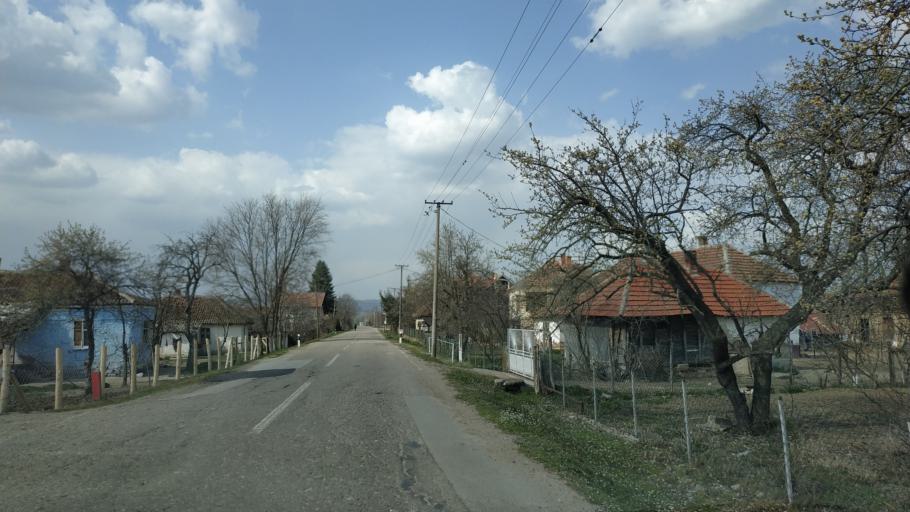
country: RS
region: Central Serbia
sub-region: Nisavski Okrug
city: Razanj
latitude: 43.5855
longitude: 21.5704
